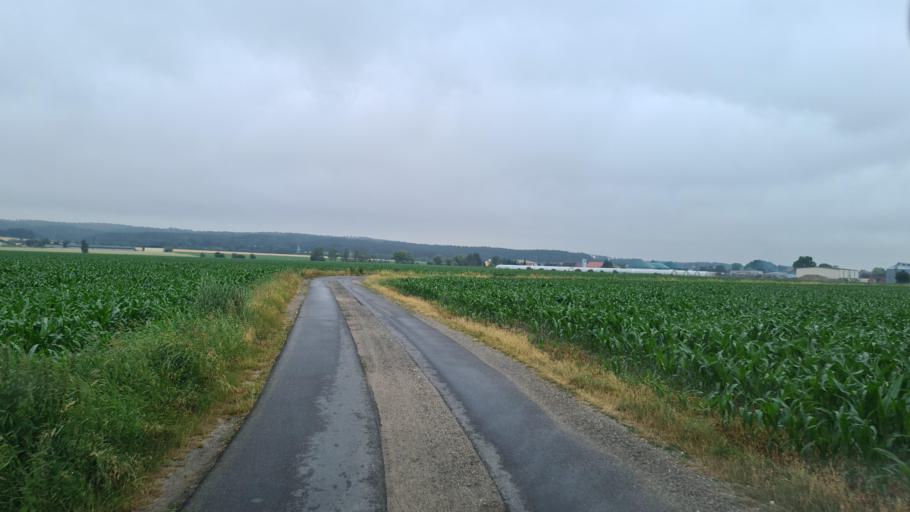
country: DE
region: Brandenburg
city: Grosskmehlen
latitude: 51.3902
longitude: 13.7208
